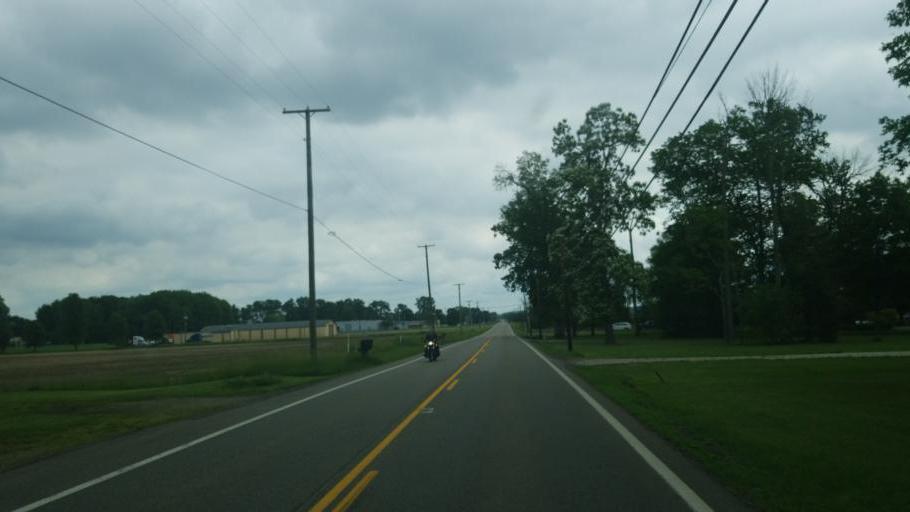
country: US
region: Ohio
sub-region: Fairfield County
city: Baltimore
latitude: 39.8417
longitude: -82.5857
